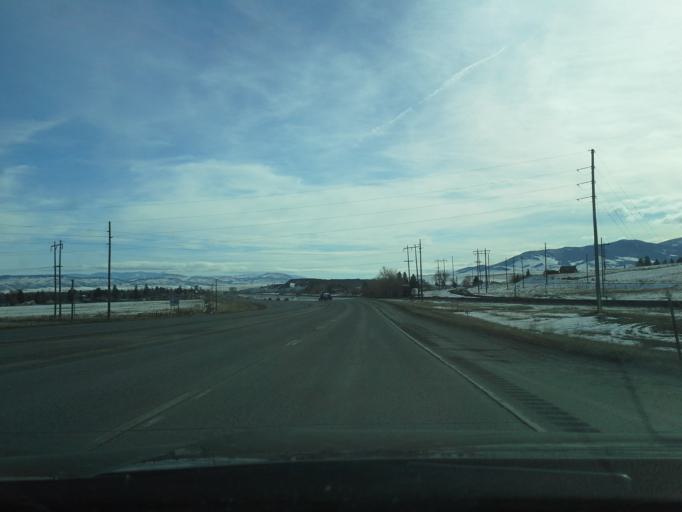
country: US
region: Montana
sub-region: Lewis and Clark County
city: East Helena
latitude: 46.5911
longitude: -111.9410
